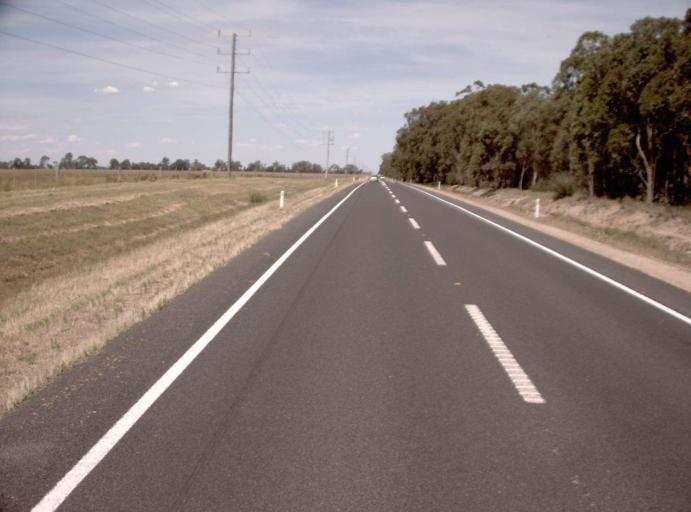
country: AU
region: Victoria
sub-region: East Gippsland
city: Bairnsdale
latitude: -37.8759
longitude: 147.4456
